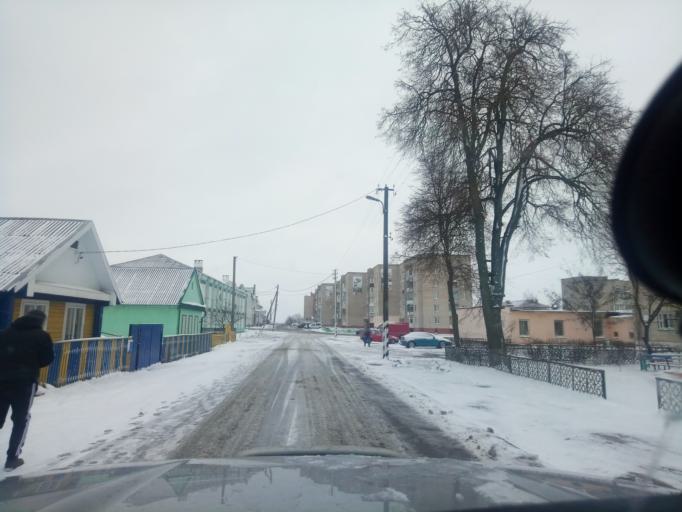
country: BY
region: Minsk
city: Kapyl'
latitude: 53.1521
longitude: 27.0842
